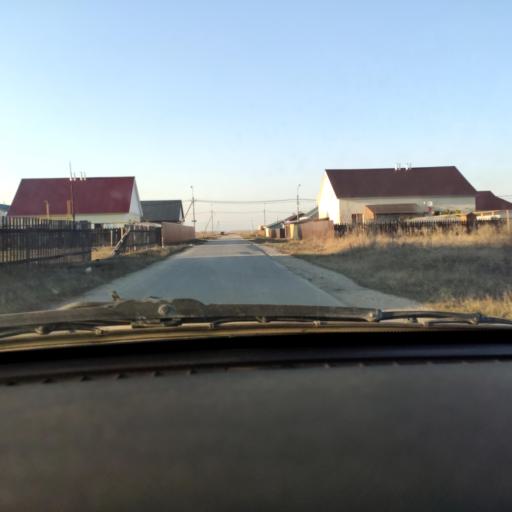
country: RU
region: Samara
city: Podstepki
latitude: 53.5750
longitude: 49.1134
